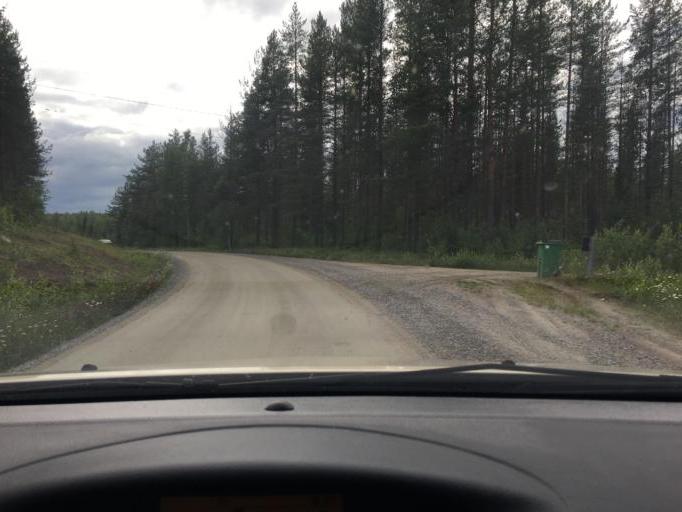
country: SE
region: Norrbotten
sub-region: Overkalix Kommun
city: OEverkalix
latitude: 66.0922
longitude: 22.8245
